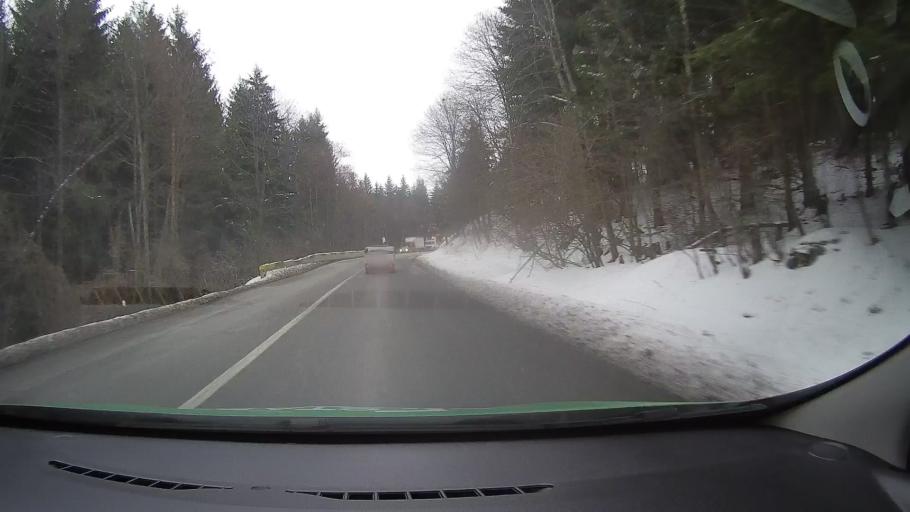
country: RO
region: Brasov
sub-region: Oras Predeal
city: Predeal
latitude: 45.5181
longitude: 25.5019
